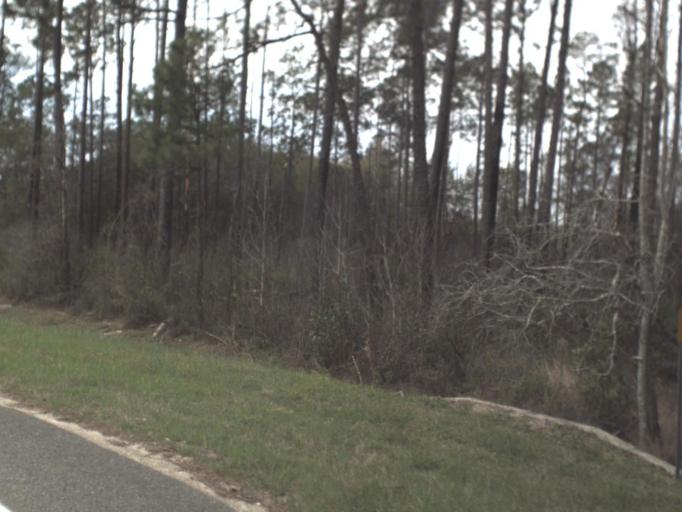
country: US
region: Florida
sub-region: Liberty County
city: Bristol
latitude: 30.4525
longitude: -84.9678
